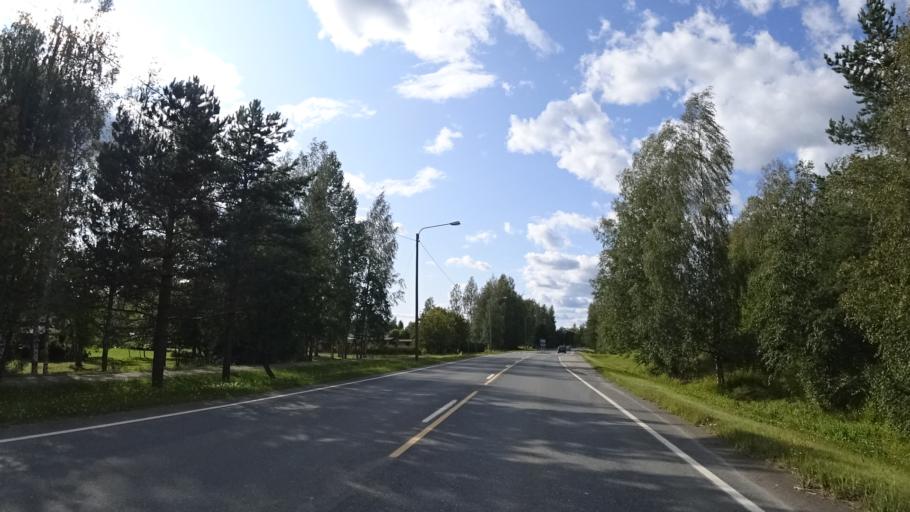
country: FI
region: North Karelia
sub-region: Keski-Karjala
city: Tohmajaervi
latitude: 62.2232
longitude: 30.3431
